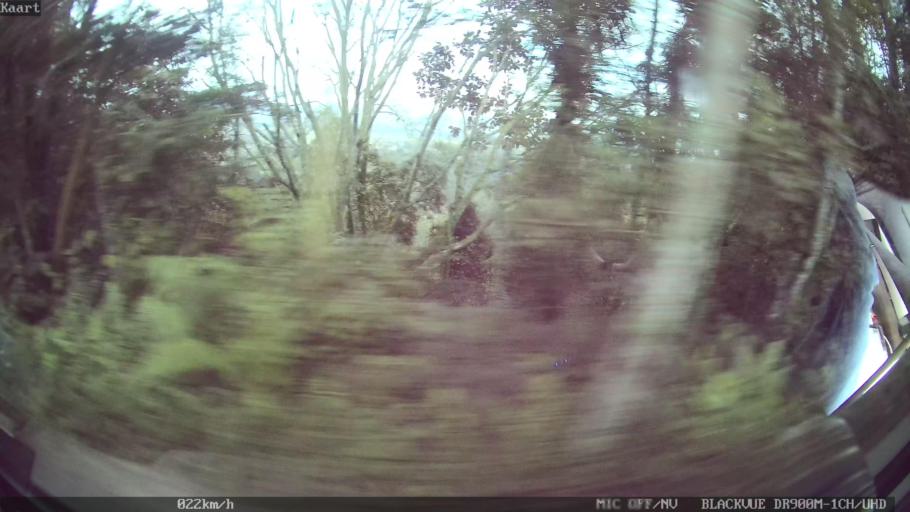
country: ID
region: Bali
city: Peneng
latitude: -8.3612
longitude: 115.2073
